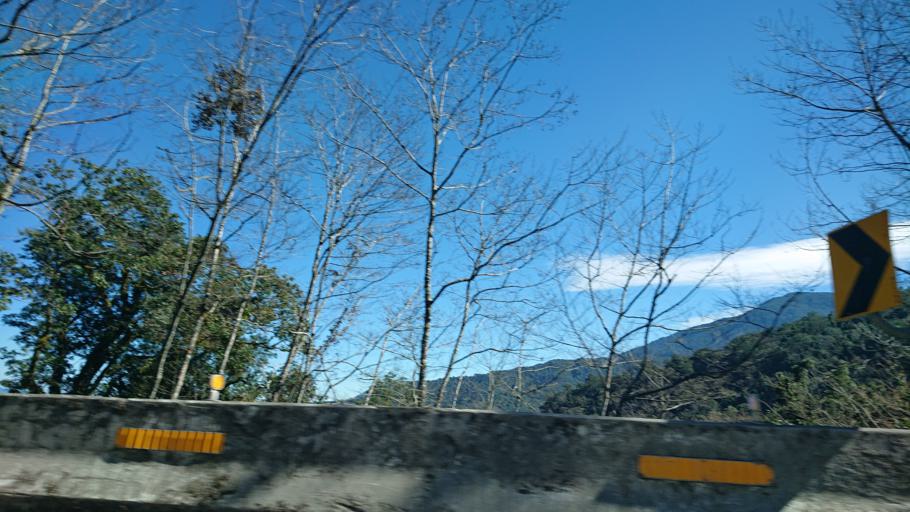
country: TW
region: Taiwan
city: Daxi
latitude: 24.4064
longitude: 121.3670
